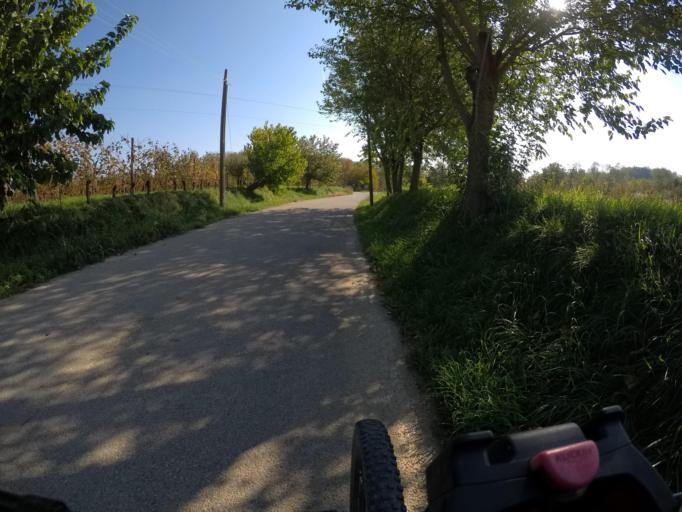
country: IT
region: Friuli Venezia Giulia
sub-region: Provincia di Udine
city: Buttrio
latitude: 46.0185
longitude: 13.3492
